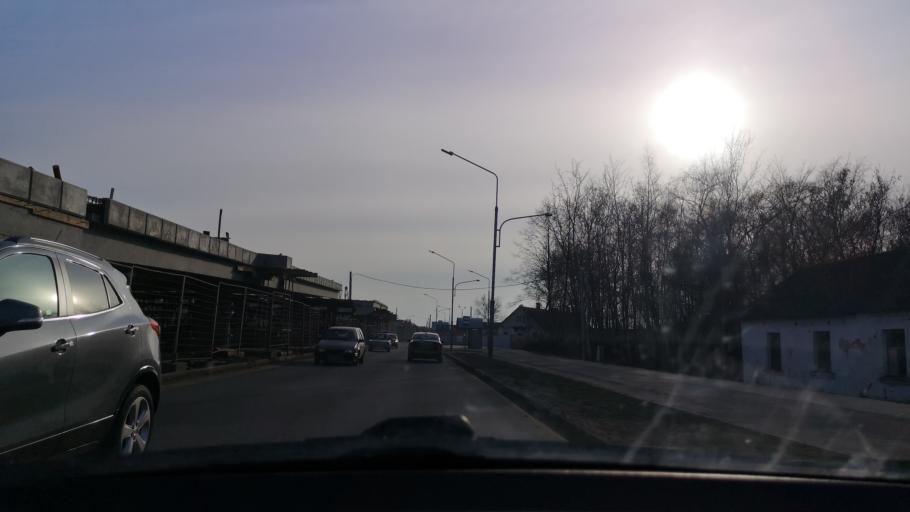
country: BY
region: Brest
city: Brest
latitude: 52.1096
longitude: 23.6670
